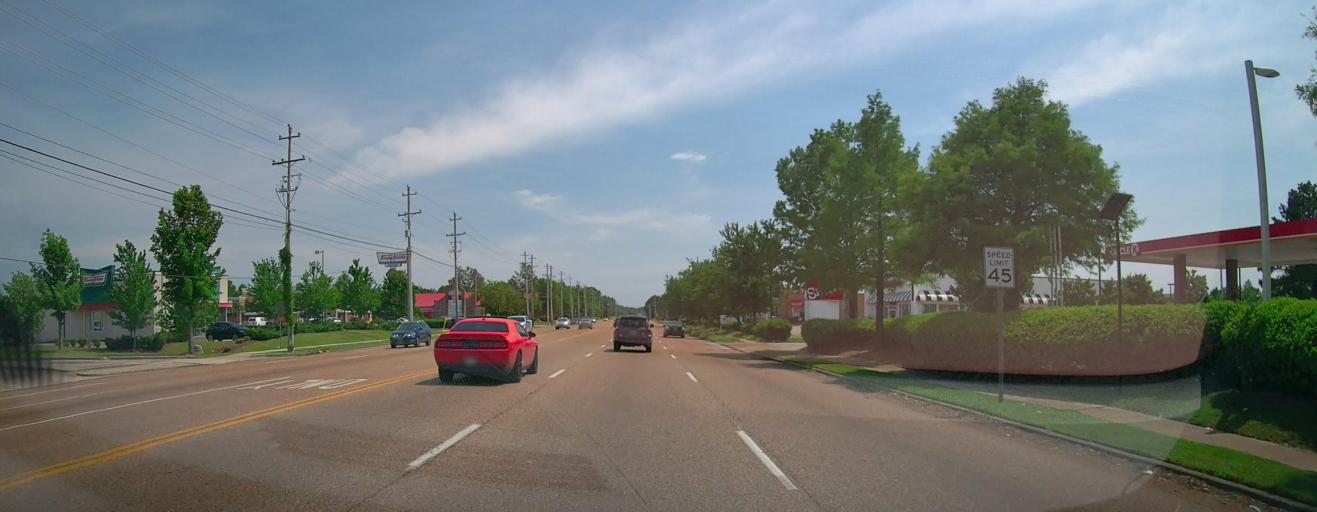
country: US
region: Tennessee
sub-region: Shelby County
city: Germantown
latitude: 35.0349
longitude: -89.7959
